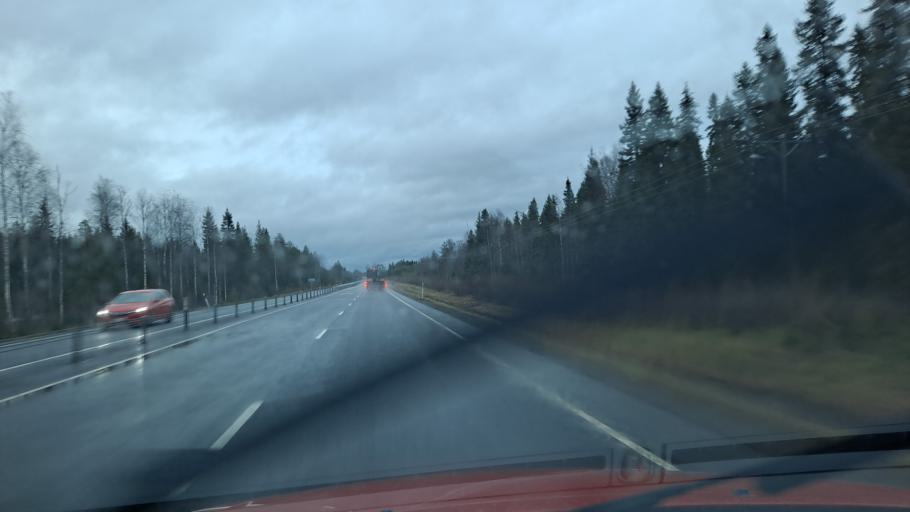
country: FI
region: Lapland
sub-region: Kemi-Tornio
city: Simo
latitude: 65.6667
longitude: 24.9790
